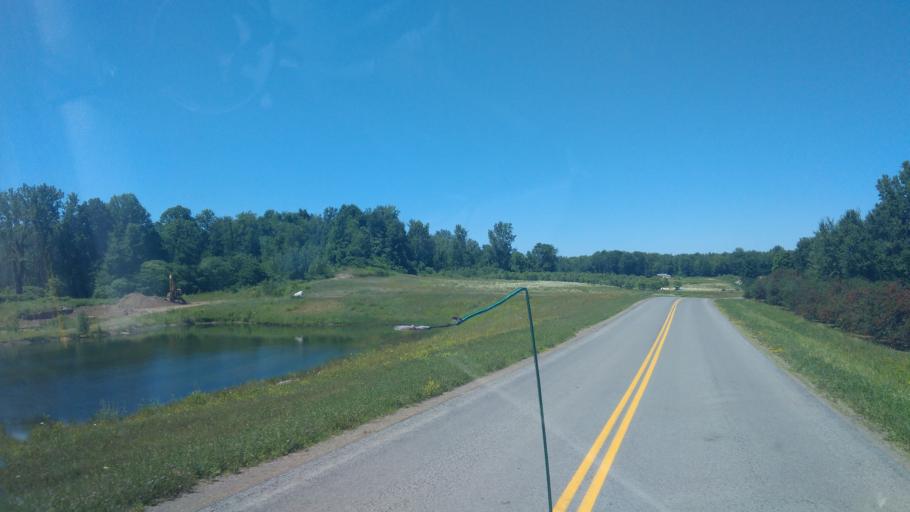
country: US
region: New York
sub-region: Wayne County
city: Lyons
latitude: 43.1599
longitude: -76.9796
